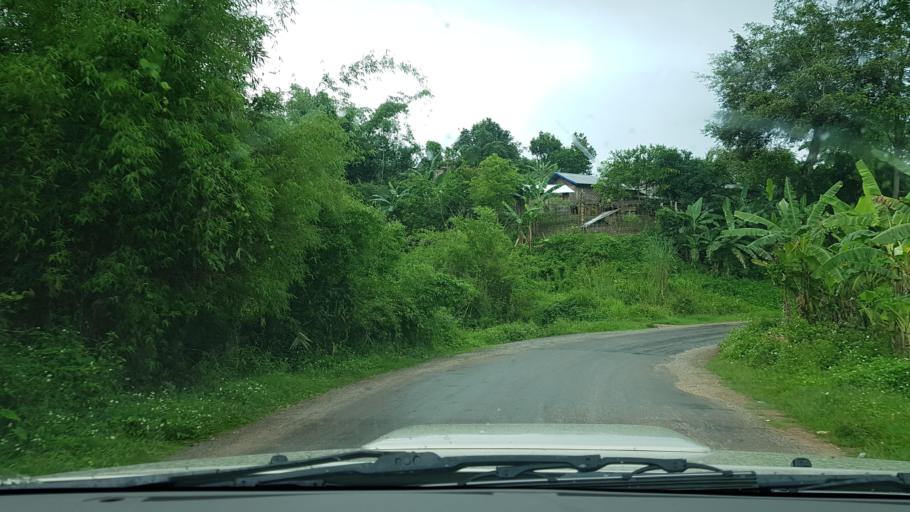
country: LA
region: Oudomxai
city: Muang Xay
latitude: 20.5850
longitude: 101.9251
